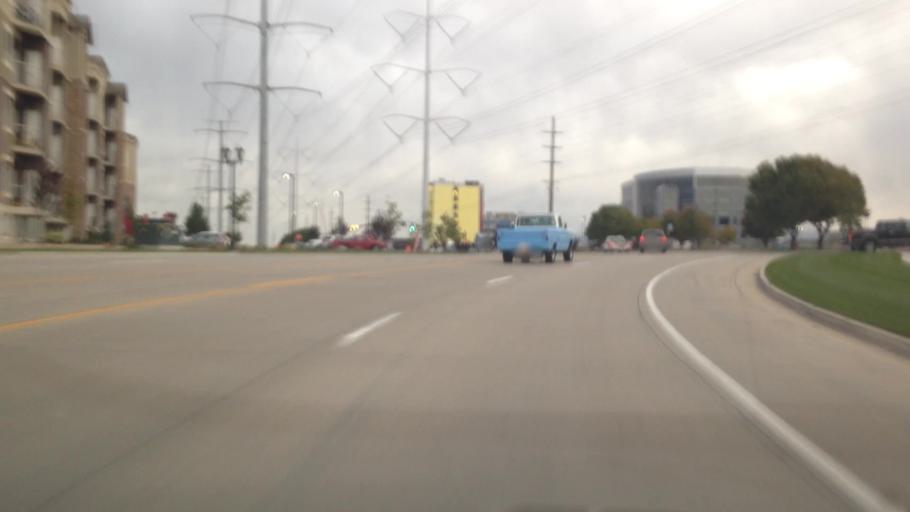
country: US
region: Utah
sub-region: Salt Lake County
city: South Jordan
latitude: 40.5610
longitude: -111.9027
